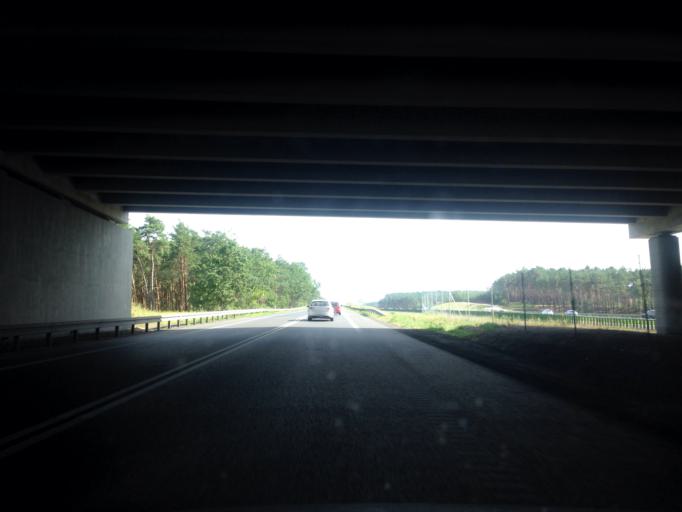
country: PL
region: Kujawsko-Pomorskie
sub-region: Powiat aleksandrowski
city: Aleksandrow Kujawski
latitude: 52.9334
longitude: 18.7042
